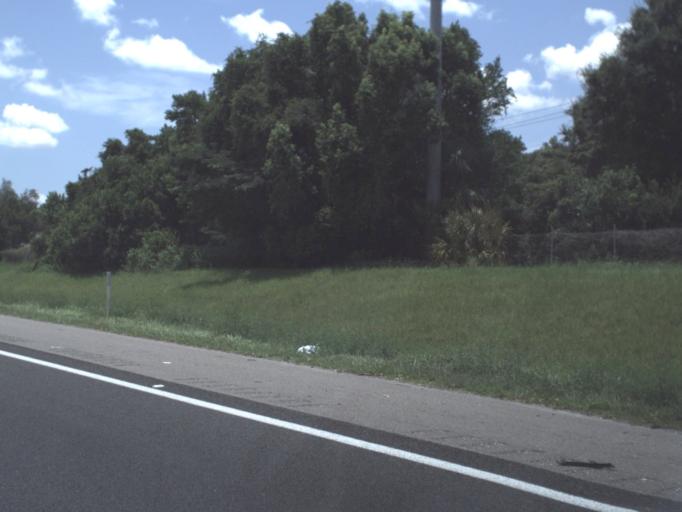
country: US
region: Florida
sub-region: Hillsborough County
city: Temple Terrace
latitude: 28.0438
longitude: -82.3519
